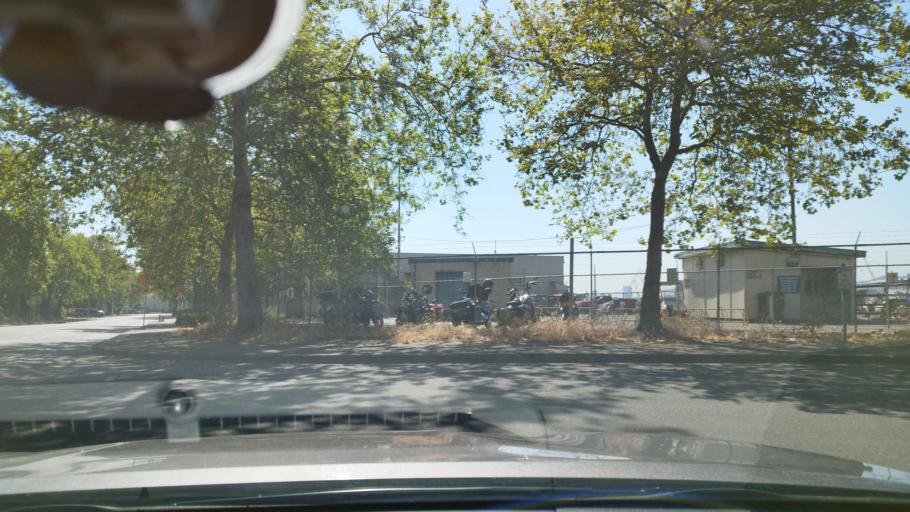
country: US
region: Oregon
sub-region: Multnomah County
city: Portland
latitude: 45.5631
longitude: -122.7194
